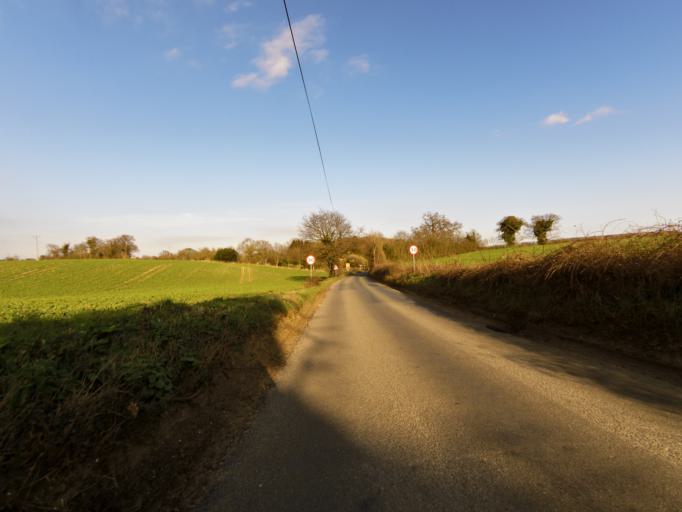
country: GB
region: England
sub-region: Suffolk
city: Kesgrave
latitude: 52.0921
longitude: 1.2346
